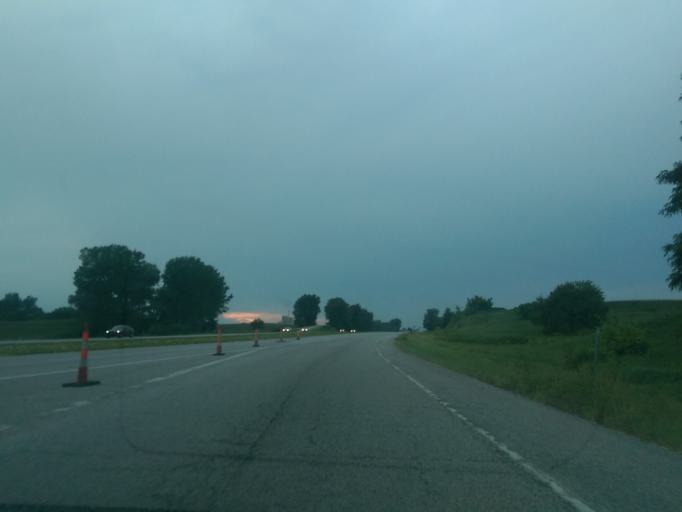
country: US
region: Missouri
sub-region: Holt County
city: Oregon
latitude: 40.0464
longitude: -95.1405
